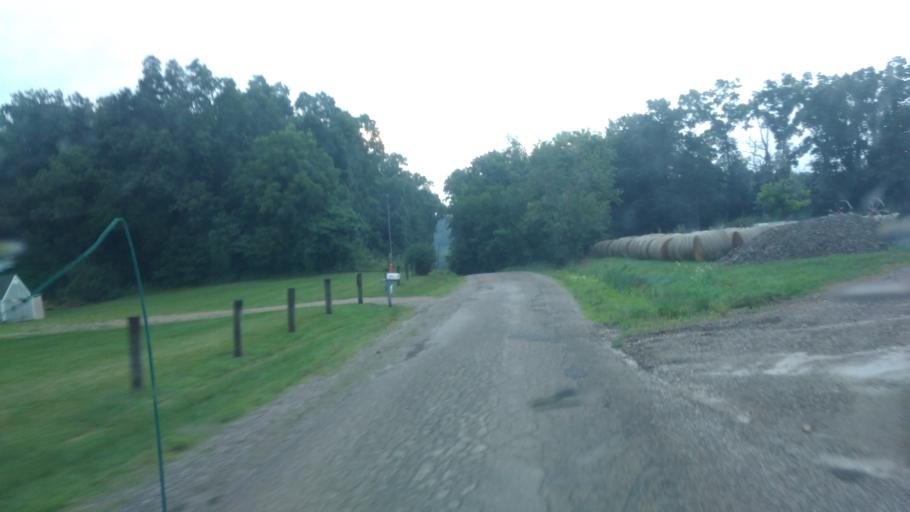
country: US
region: Ohio
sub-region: Guernsey County
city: Byesville
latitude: 40.0222
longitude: -81.3652
